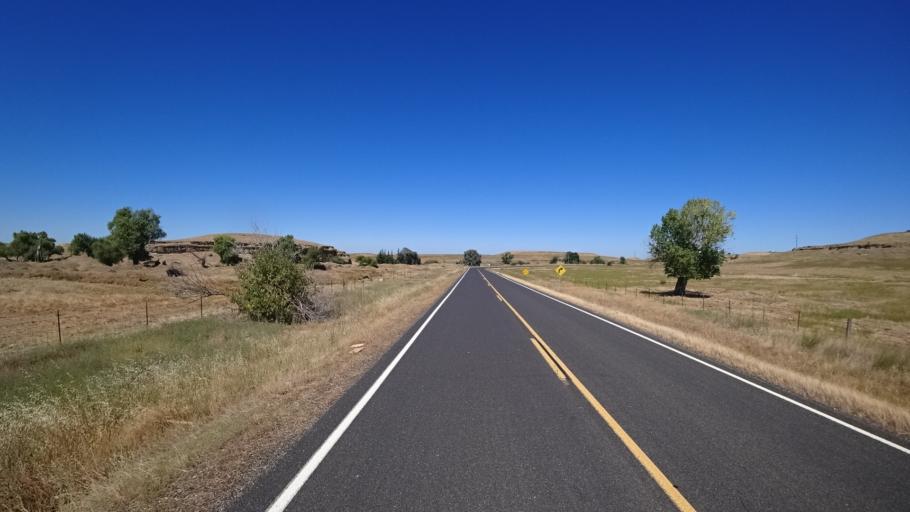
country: US
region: California
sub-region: Calaveras County
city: Rancho Calaveras
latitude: 38.0541
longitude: -120.8673
